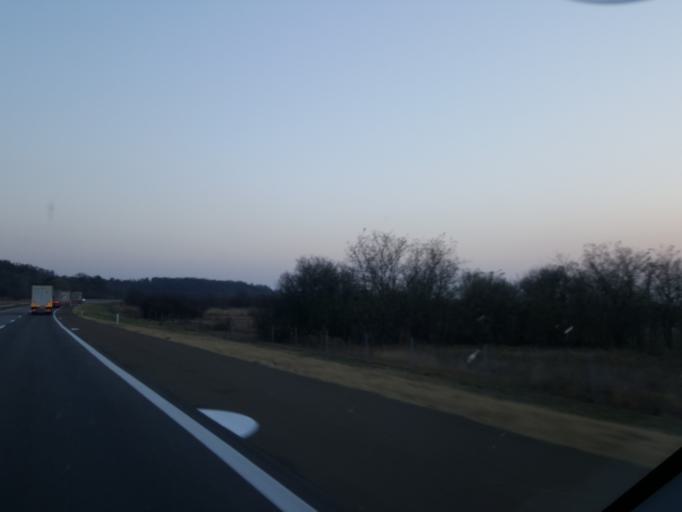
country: RS
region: Central Serbia
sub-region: Rasinski Okrug
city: Cicevac
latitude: 43.7850
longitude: 21.4371
